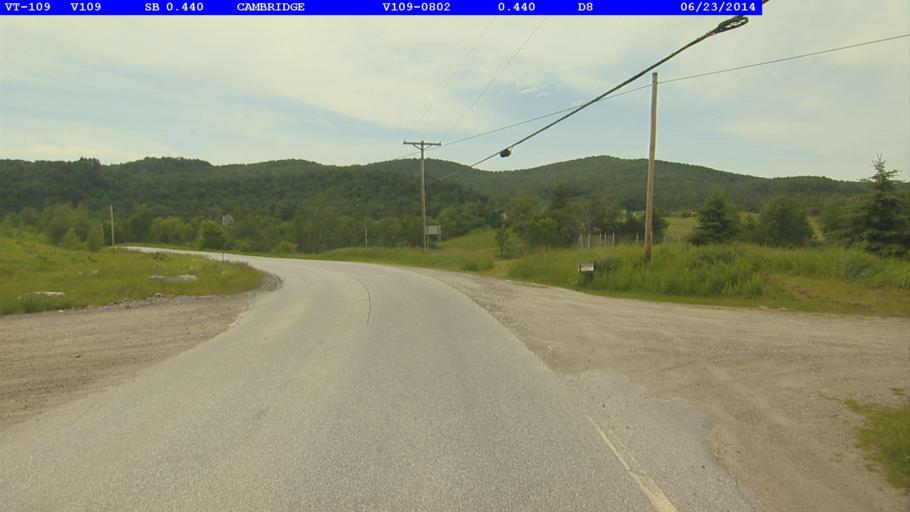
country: US
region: Vermont
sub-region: Lamoille County
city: Johnson
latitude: 44.6544
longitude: -72.8194
